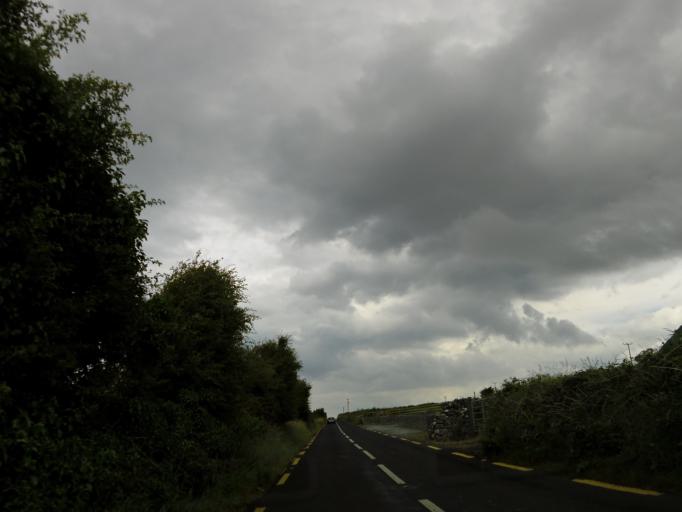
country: IE
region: Connaught
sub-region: County Galway
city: Gaillimh
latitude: 53.1244
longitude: -9.0699
